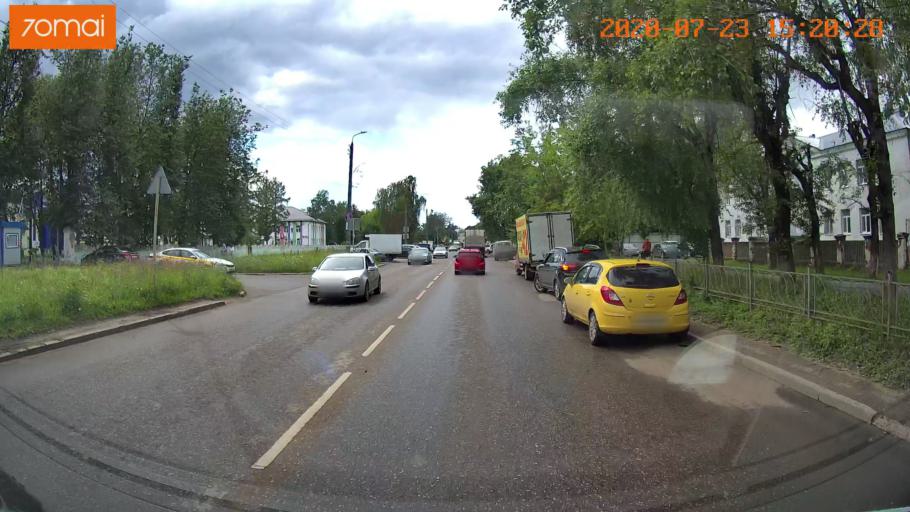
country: RU
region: Ivanovo
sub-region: Gorod Ivanovo
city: Ivanovo
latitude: 56.9722
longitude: 40.9676
